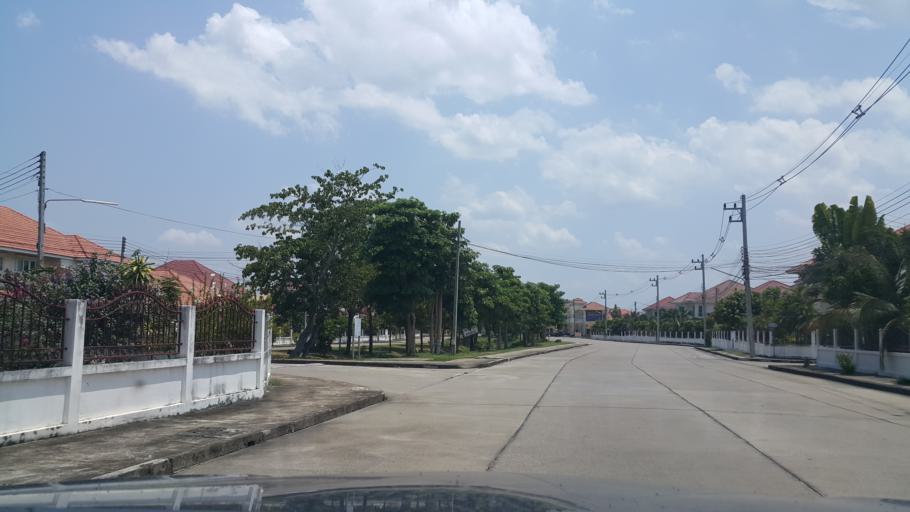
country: TH
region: Chiang Mai
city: San Kamphaeng
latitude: 18.7372
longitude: 99.0820
